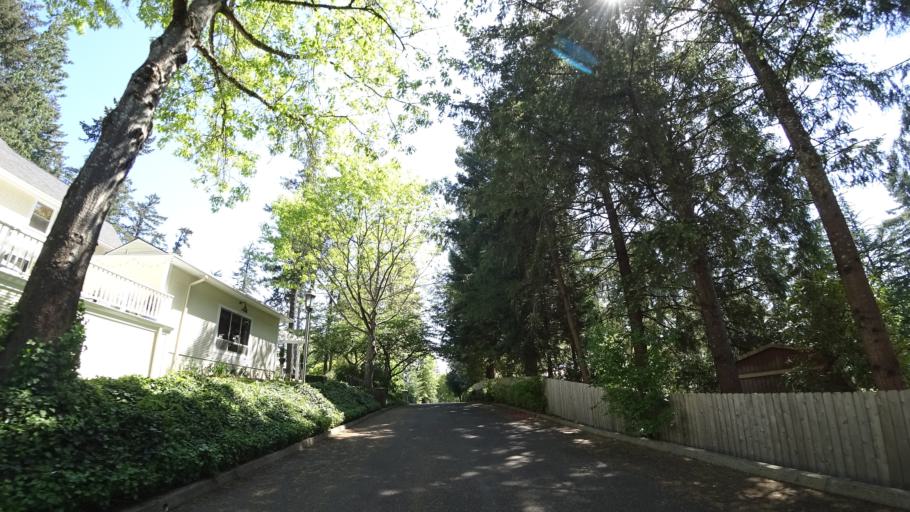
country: US
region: Oregon
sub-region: Washington County
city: Raleigh Hills
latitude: 45.4916
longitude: -122.7344
